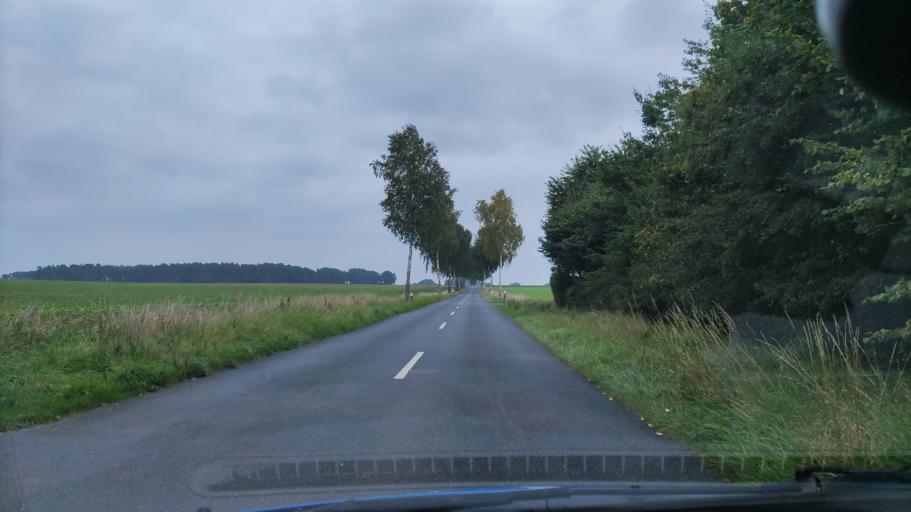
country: DE
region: Lower Saxony
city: Bienenbuttel
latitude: 53.1456
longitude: 10.5102
